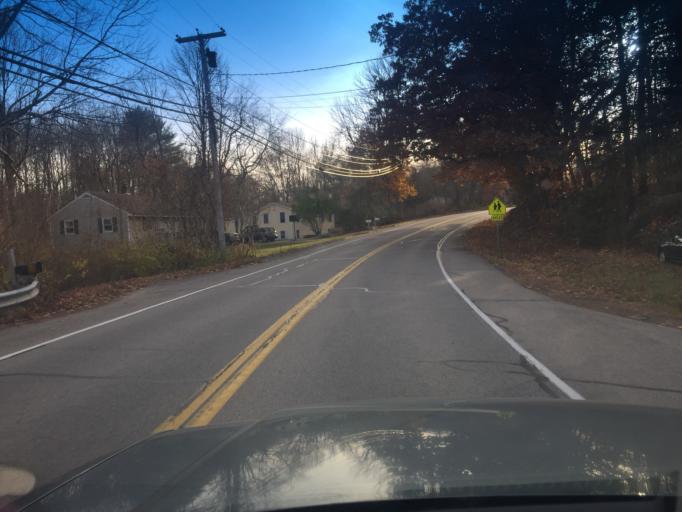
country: US
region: Maine
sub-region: York County
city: York Harbor
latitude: 43.1523
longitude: -70.6371
